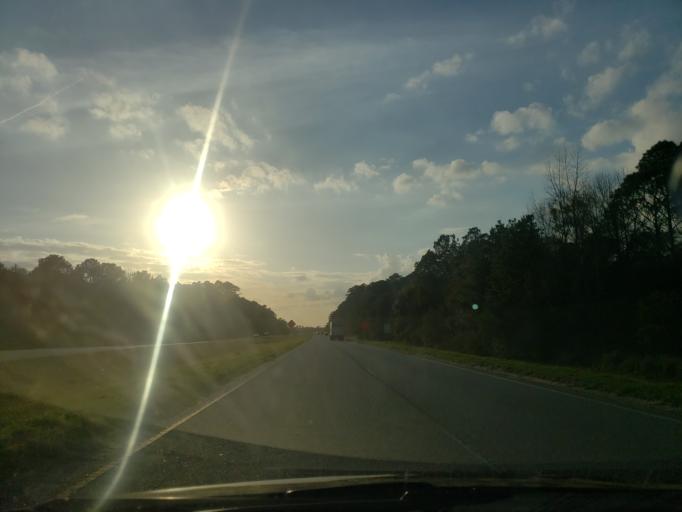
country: US
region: Georgia
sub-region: Chatham County
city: Bloomingdale
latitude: 32.1488
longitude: -81.2885
